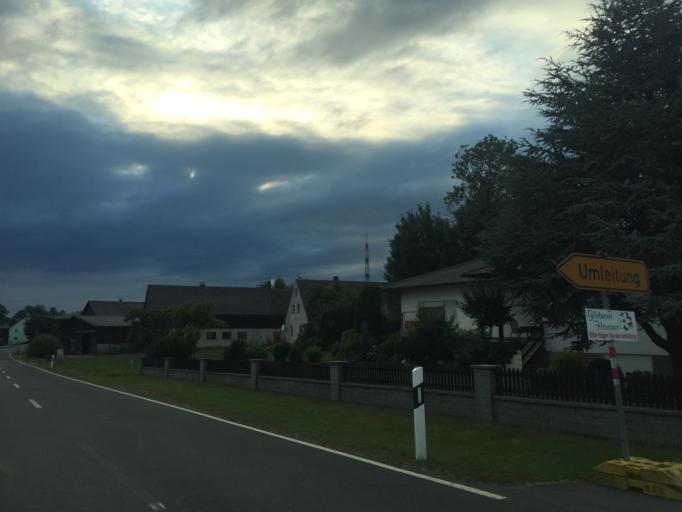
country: DE
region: Bavaria
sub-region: Upper Palatinate
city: Berg
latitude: 49.7912
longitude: 12.1283
